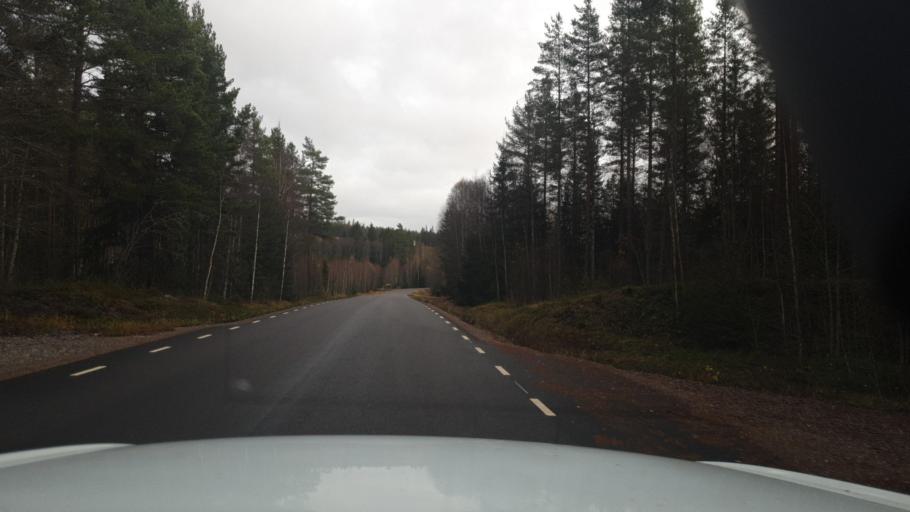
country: SE
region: Vaermland
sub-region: Torsby Kommun
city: Torsby
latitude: 59.9888
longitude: 12.7797
